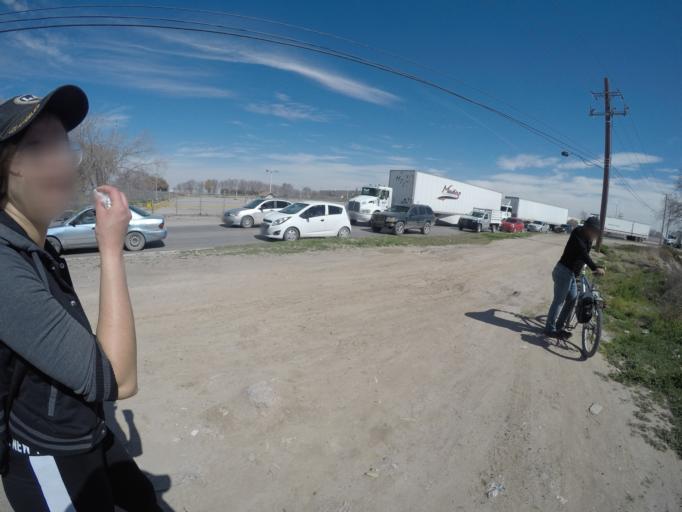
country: US
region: Texas
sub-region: El Paso County
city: Socorro
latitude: 31.6485
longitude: -106.3536
